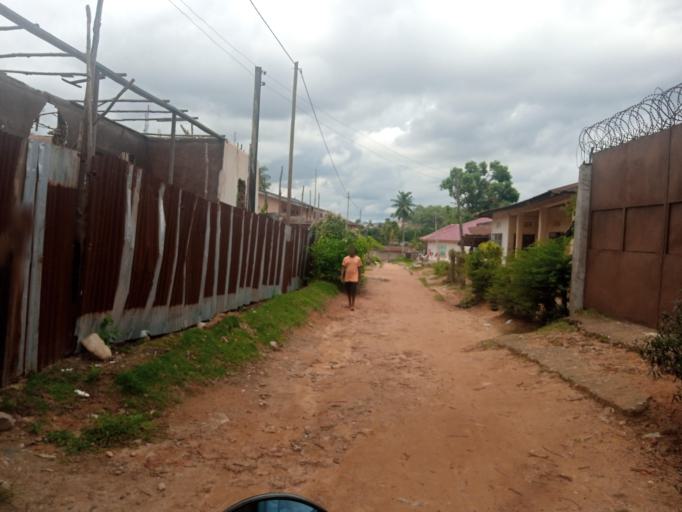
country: SL
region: Southern Province
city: Bo
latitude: 7.9541
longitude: -11.7408
